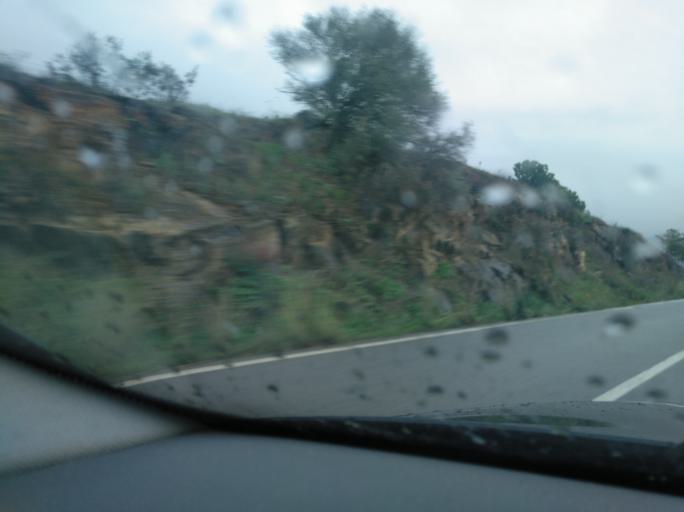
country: PT
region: Beja
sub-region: Mertola
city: Mertola
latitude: 37.5705
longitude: -7.6794
